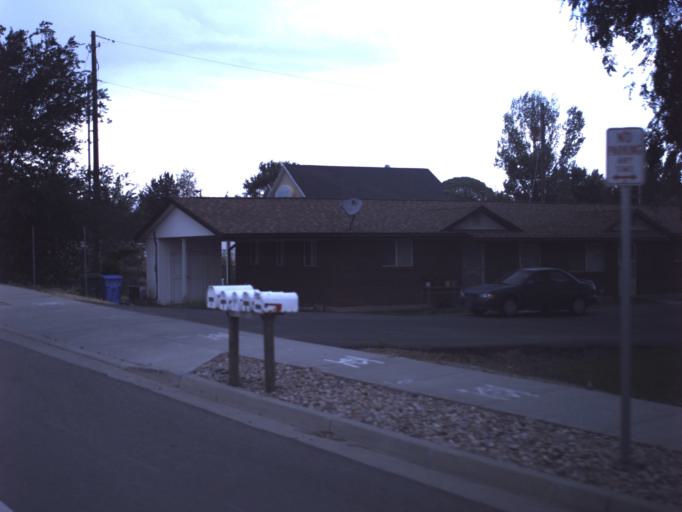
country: US
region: Utah
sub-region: Salt Lake County
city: Riverton
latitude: 40.5224
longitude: -111.9347
